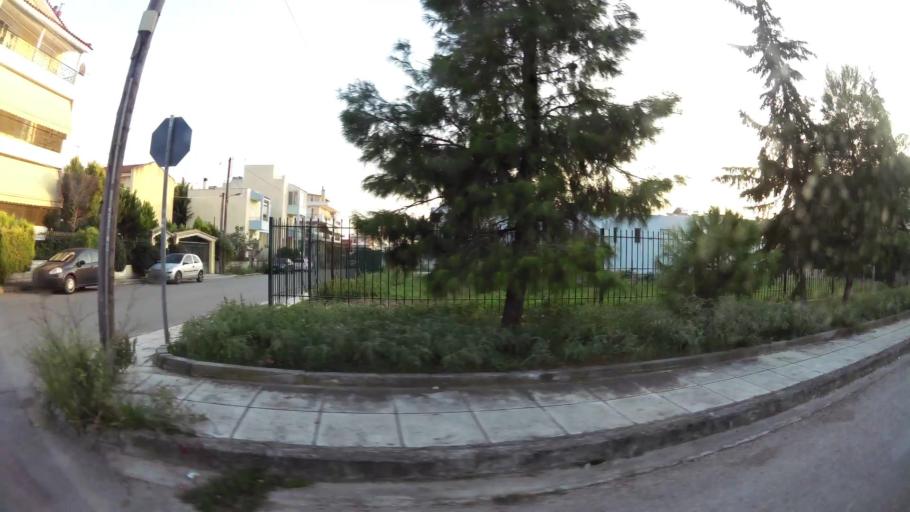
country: GR
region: Attica
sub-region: Nomarchia Anatolikis Attikis
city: Acharnes
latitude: 38.0905
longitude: 23.7460
